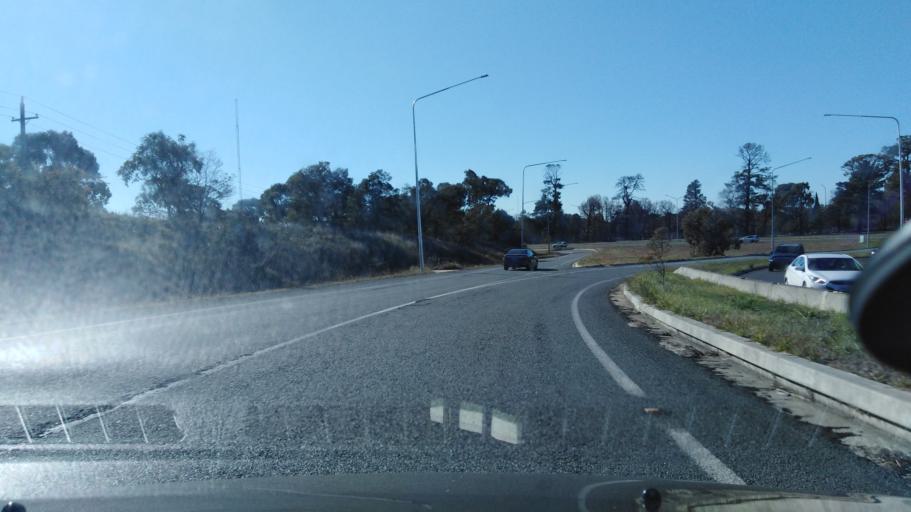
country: AU
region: Australian Capital Territory
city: Kaleen
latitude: -35.2247
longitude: 149.1200
